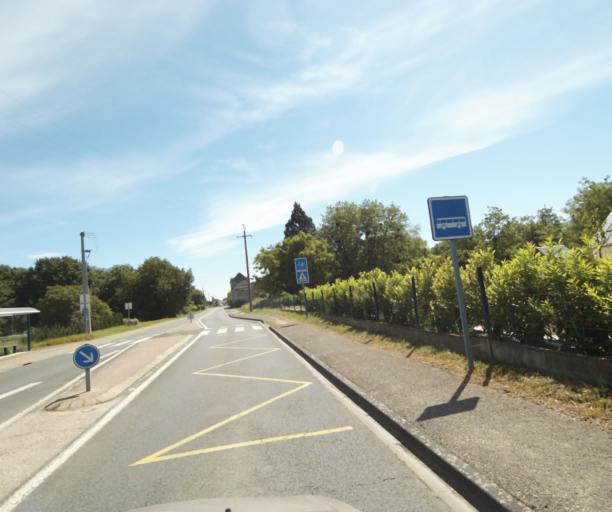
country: FR
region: Centre
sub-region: Departement d'Indre-et-Loire
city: Ligre
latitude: 47.1352
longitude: 0.3013
